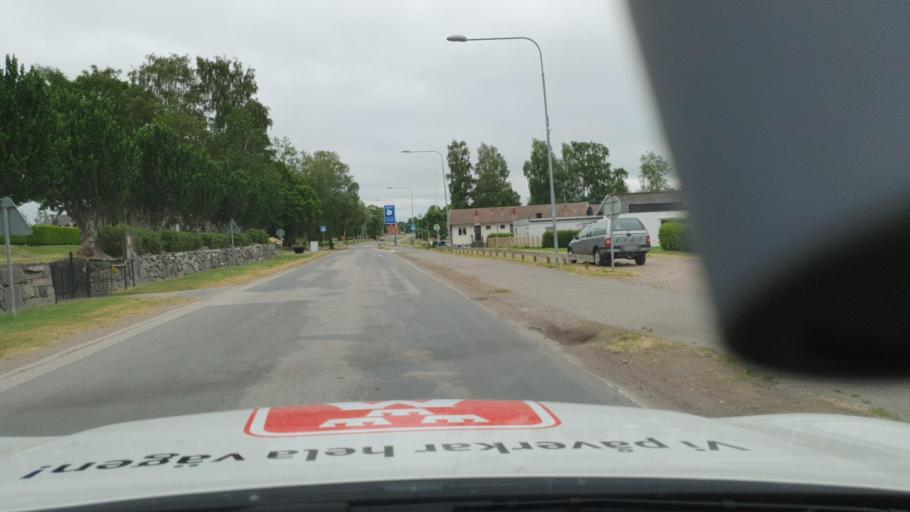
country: SE
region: Vaestra Goetaland
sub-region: Tidaholms Kommun
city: Olofstorp
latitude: 58.3514
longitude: 14.0502
